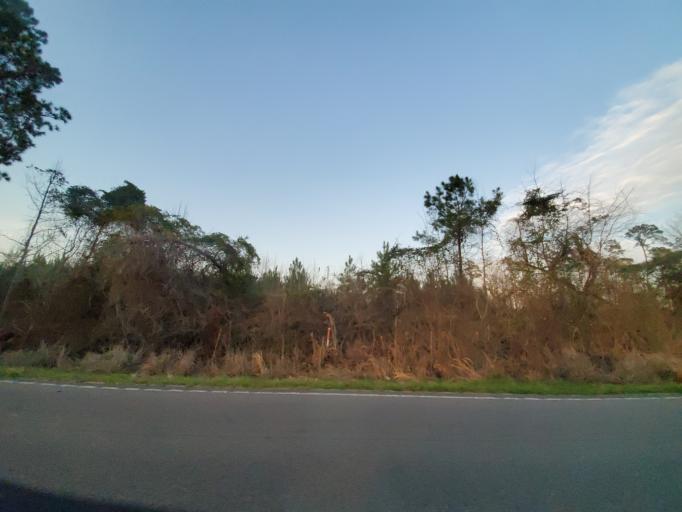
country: US
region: South Carolina
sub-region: Dorchester County
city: Ridgeville
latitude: 32.9947
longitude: -80.3121
